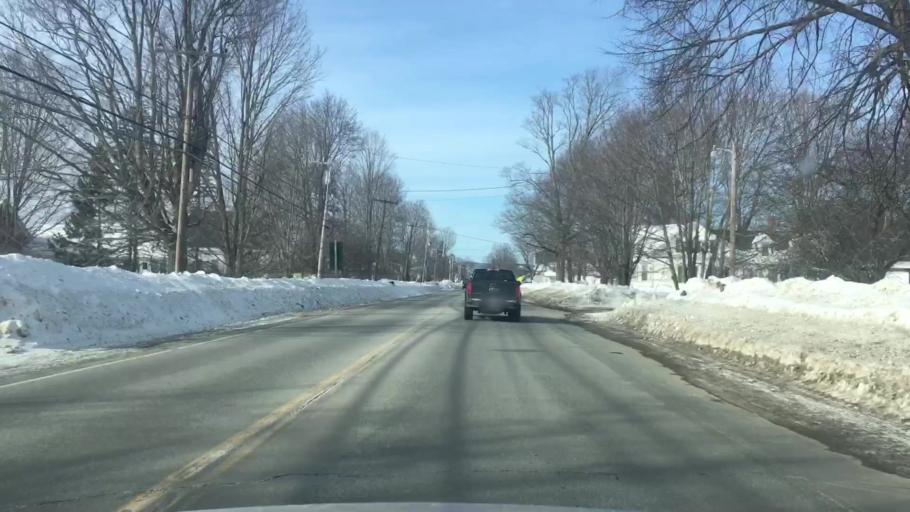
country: US
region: Maine
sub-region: Penobscot County
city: Charleston
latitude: 44.9992
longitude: -69.0213
